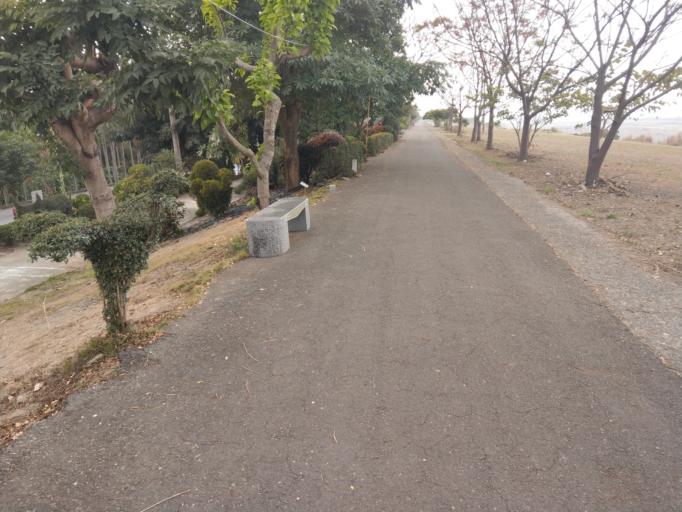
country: TW
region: Taiwan
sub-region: Pingtung
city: Pingtung
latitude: 22.7824
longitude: 120.5382
